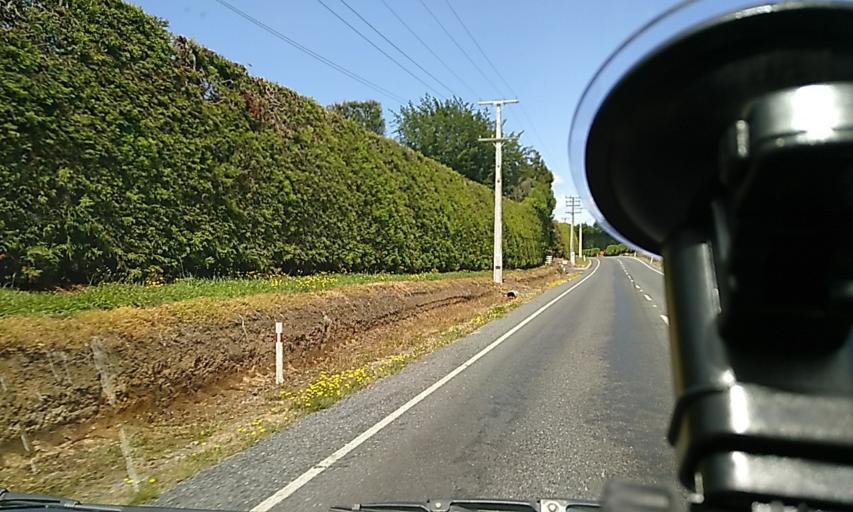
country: NZ
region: Bay of Plenty
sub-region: Western Bay of Plenty District
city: Waihi Beach
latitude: -37.4495
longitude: 175.9513
